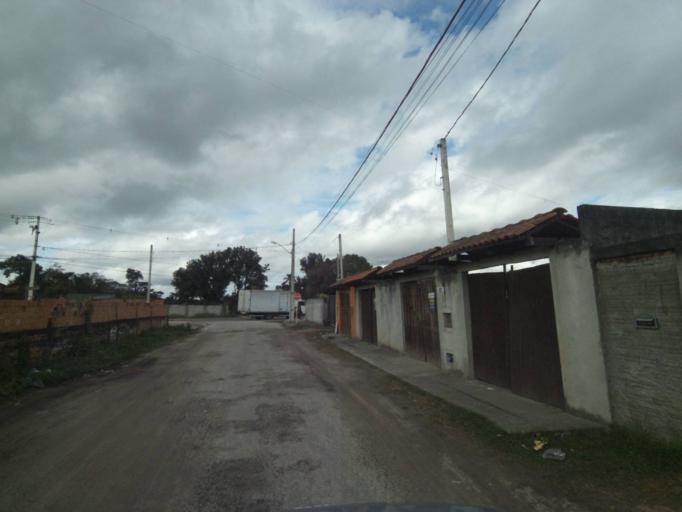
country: BR
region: Parana
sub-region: Paranagua
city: Paranagua
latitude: -25.5717
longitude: -48.5648
